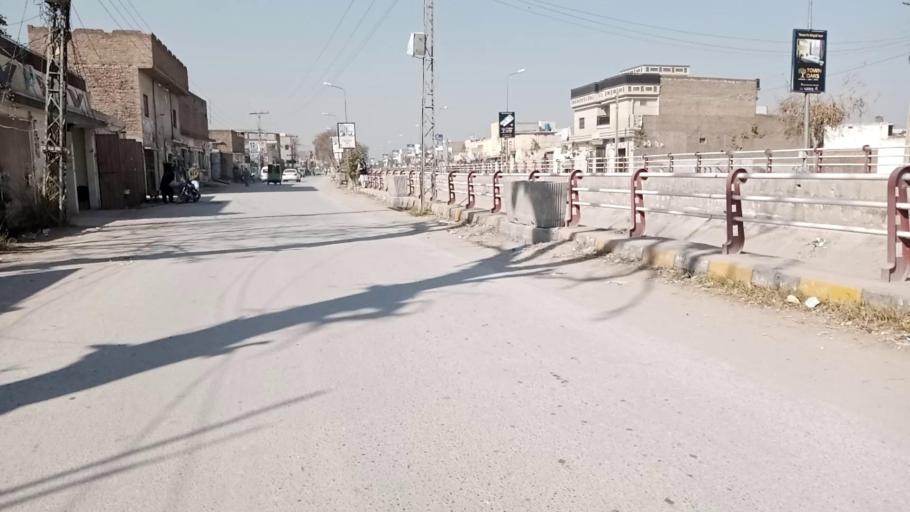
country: PK
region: Khyber Pakhtunkhwa
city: Peshawar
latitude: 33.9788
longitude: 71.5066
